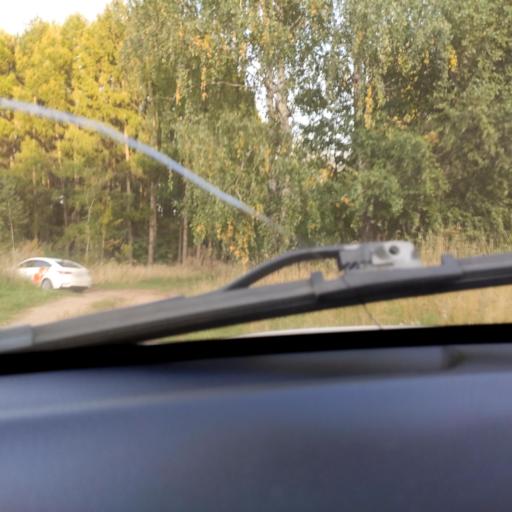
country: RU
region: Tatarstan
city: Verkhniy Uslon
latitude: 55.6600
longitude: 48.9596
